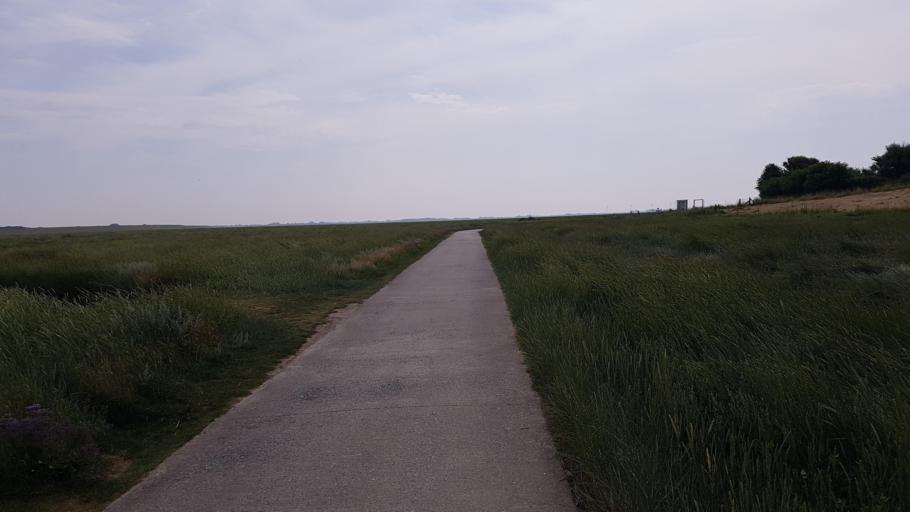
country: DE
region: Schleswig-Holstein
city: Westerhever
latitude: 54.3742
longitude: 8.6393
